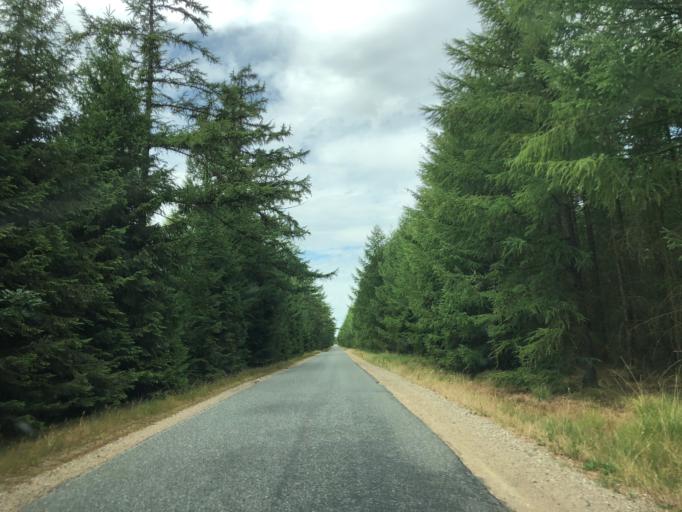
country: DK
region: South Denmark
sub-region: Billund Kommune
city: Grindsted
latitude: 55.6472
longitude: 8.9032
